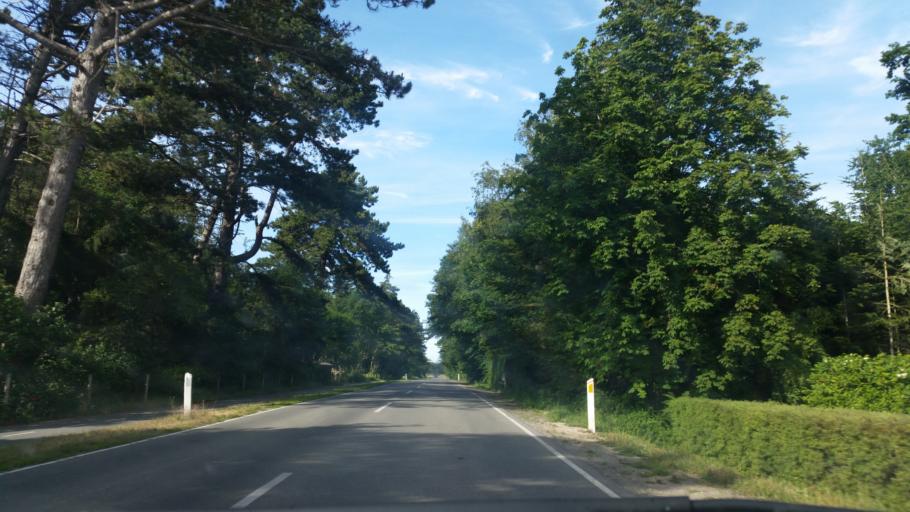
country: DK
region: Central Jutland
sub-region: Samso Kommune
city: Tranebjerg
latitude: 55.8637
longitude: 10.5791
